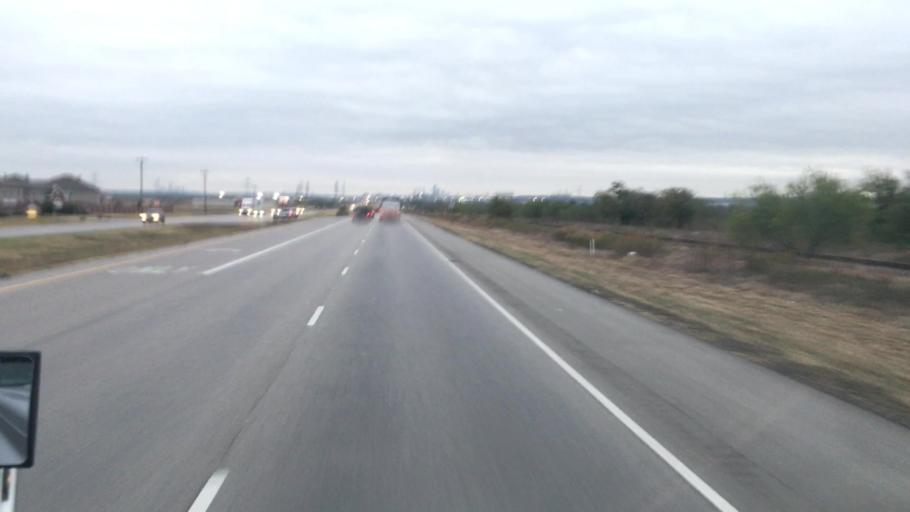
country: US
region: Texas
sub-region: Johnson County
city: Venus
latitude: 32.4397
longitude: -97.0914
